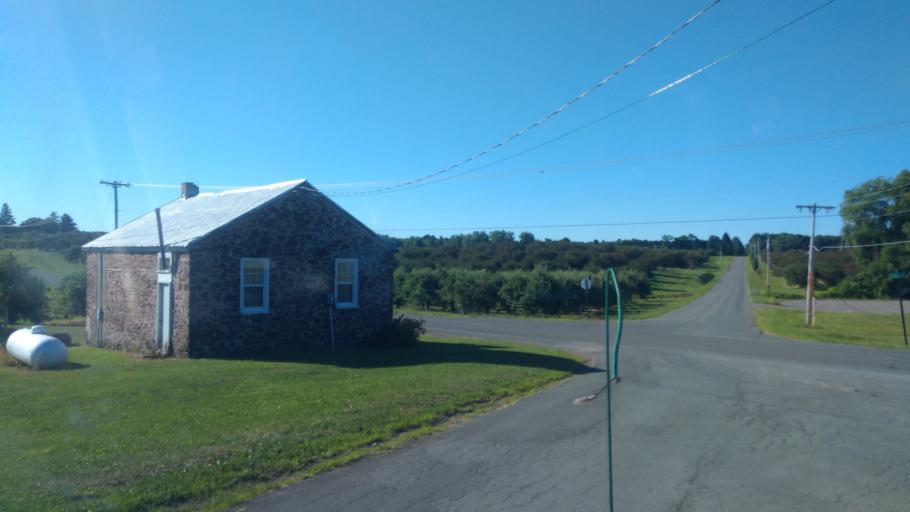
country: US
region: New York
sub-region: Wayne County
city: Sodus
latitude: 43.2757
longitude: -77.1135
